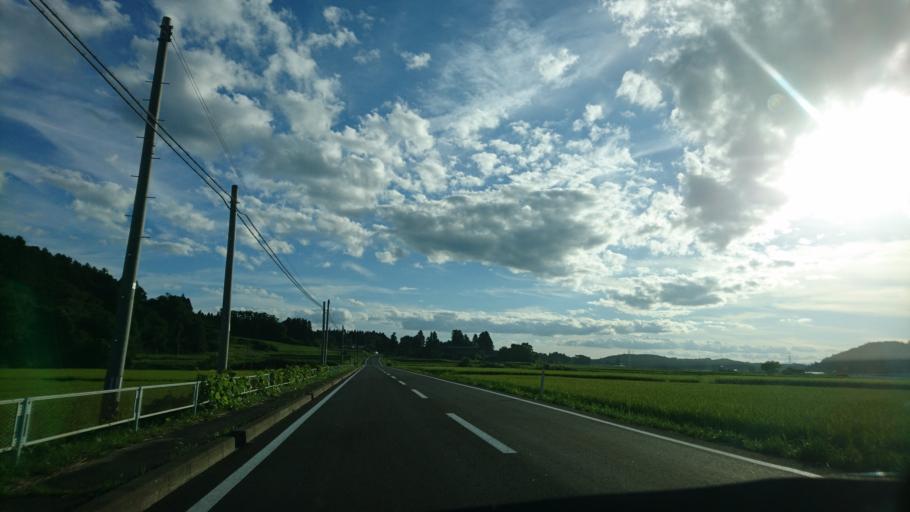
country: JP
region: Iwate
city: Ichinoseki
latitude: 38.8436
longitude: 141.1541
